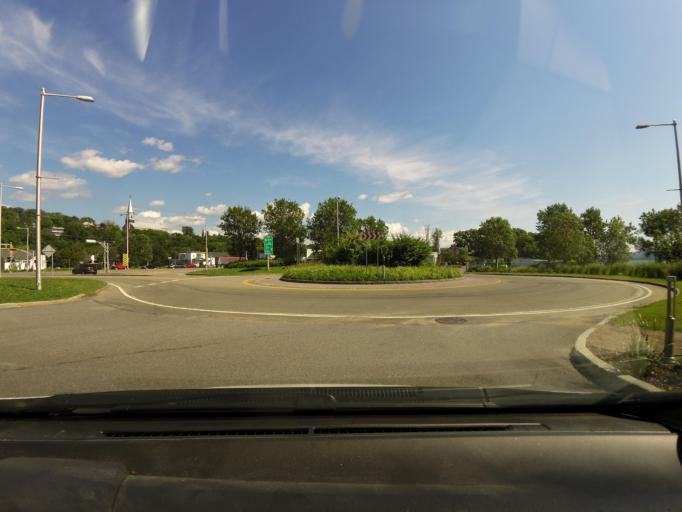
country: CA
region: Quebec
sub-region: Capitale-Nationale
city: Chateau-Richer
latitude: 46.9119
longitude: -71.0935
